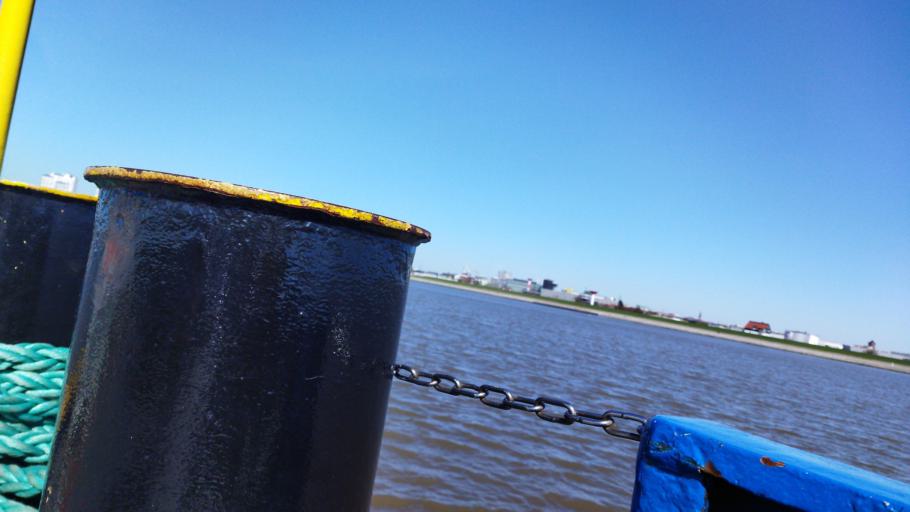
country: DE
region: Bremen
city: Bremerhaven
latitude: 53.5294
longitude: 8.5675
